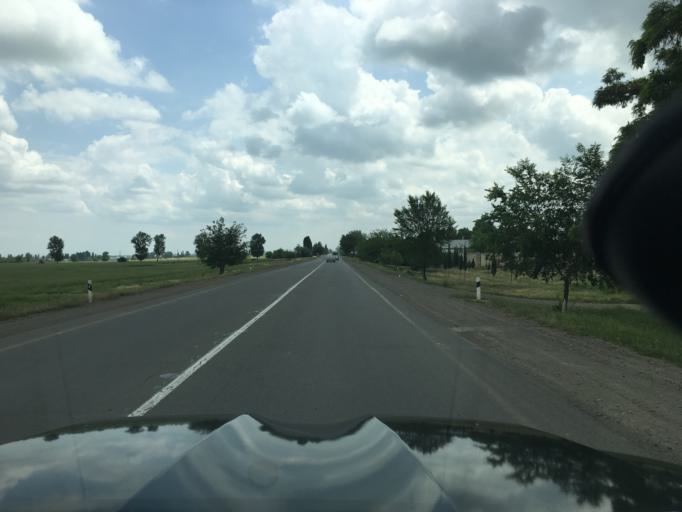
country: AZ
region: Tovuz
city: Tovuz
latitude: 40.9579
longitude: 45.7291
